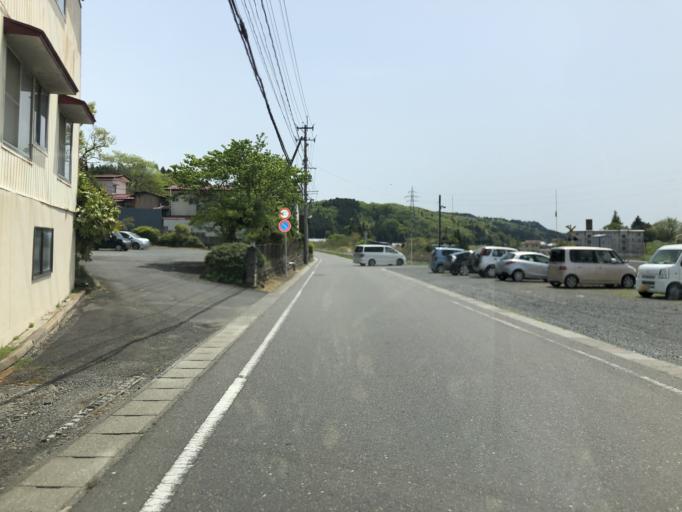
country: JP
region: Fukushima
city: Ishikawa
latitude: 37.0308
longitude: 140.3909
